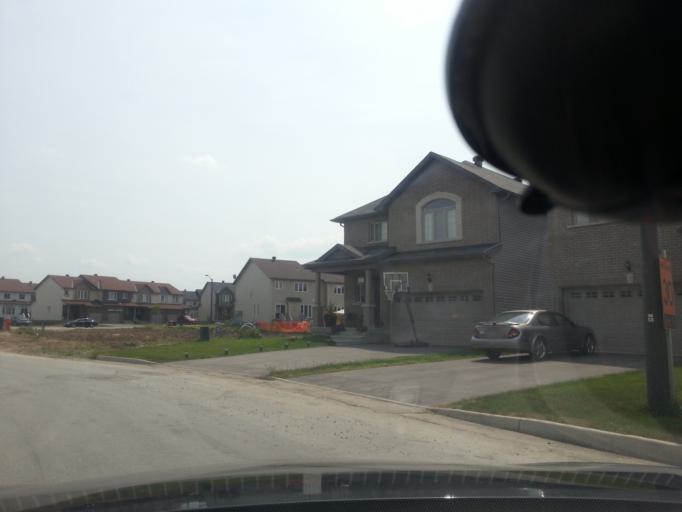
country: CA
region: Ontario
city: Bells Corners
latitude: 45.2656
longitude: -75.6986
